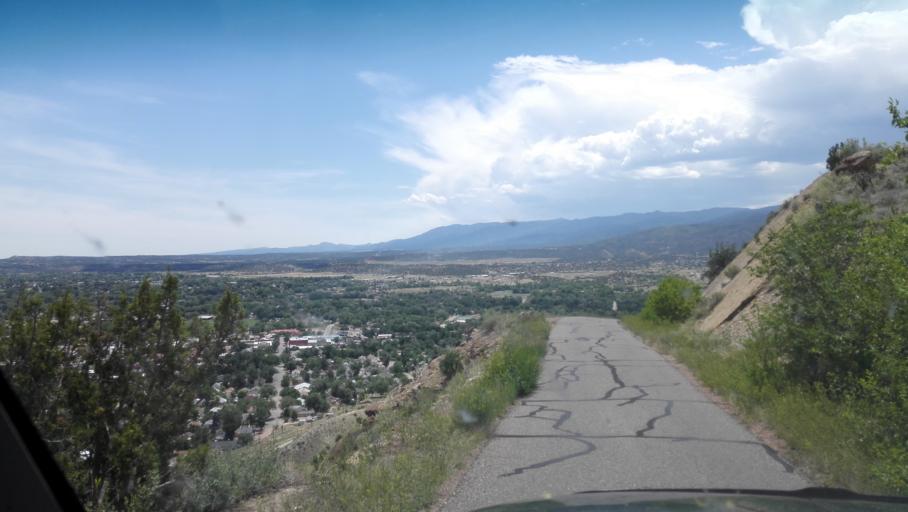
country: US
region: Colorado
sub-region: Fremont County
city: Canon City
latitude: 38.4489
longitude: -105.2490
